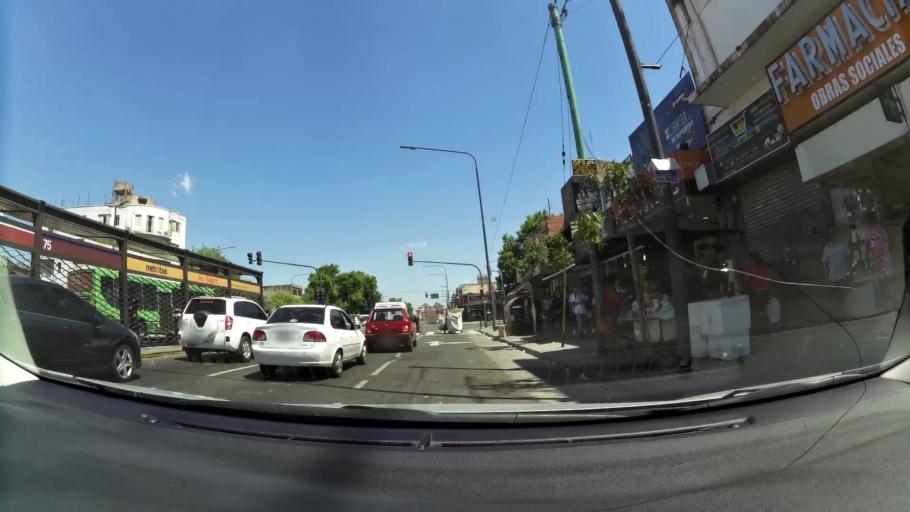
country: AR
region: Buenos Aires
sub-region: Partido de Avellaneda
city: Avellaneda
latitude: -34.6543
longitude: -58.4166
